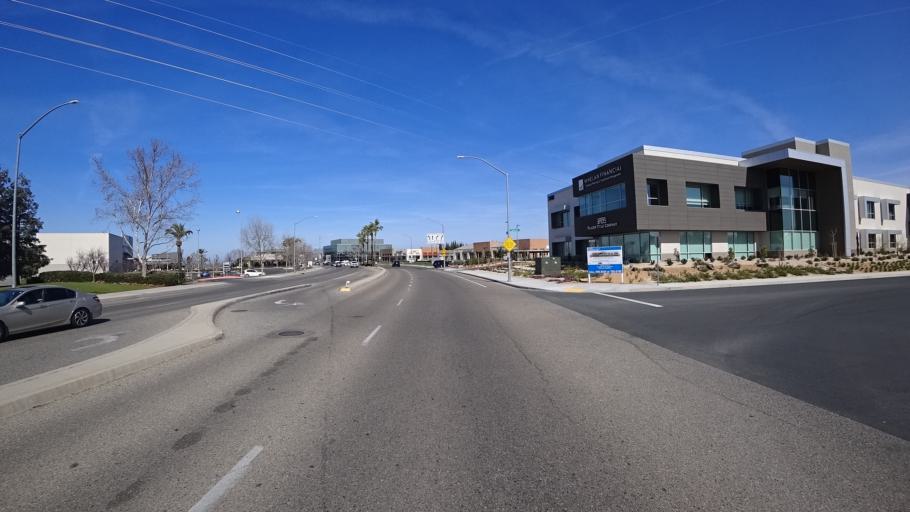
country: US
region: California
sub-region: Fresno County
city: Clovis
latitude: 36.8497
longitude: -119.8060
